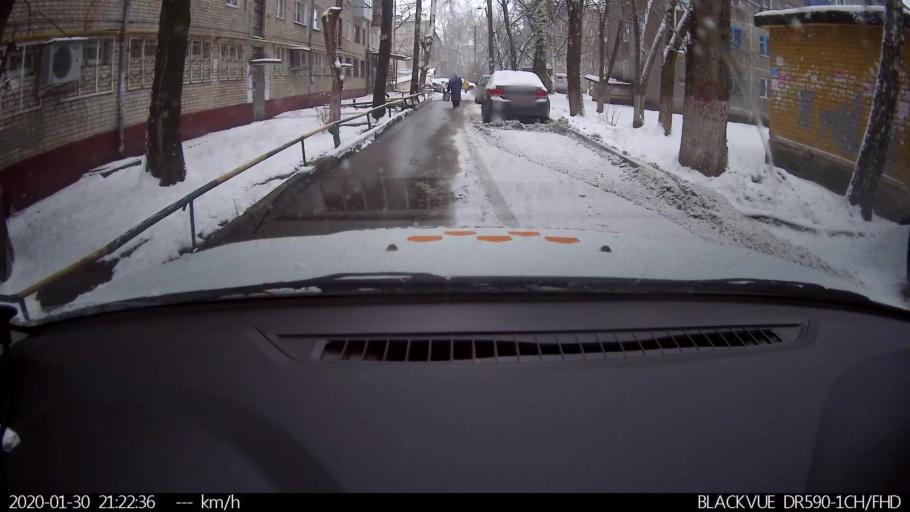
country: RU
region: Nizjnij Novgorod
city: Gorbatovka
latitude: 56.2332
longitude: 43.8528
